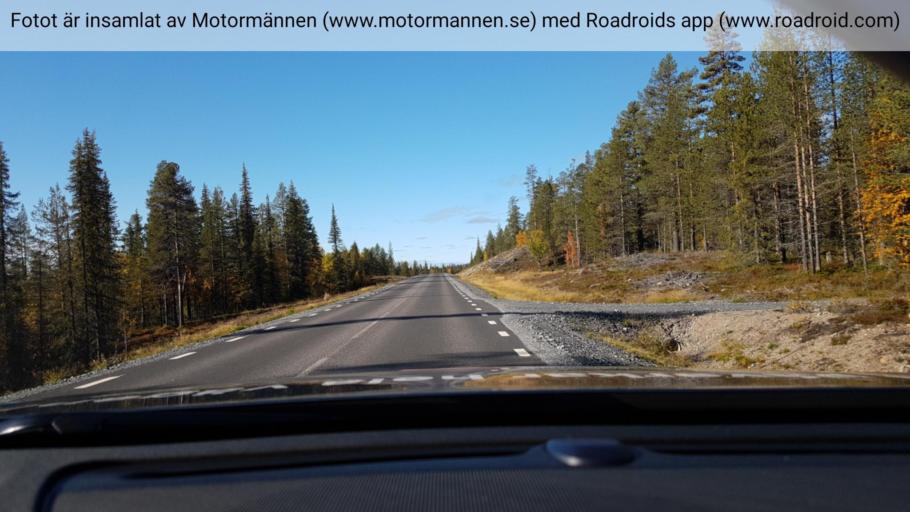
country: SE
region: Norrbotten
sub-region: Gallivare Kommun
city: Gaellivare
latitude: 66.9377
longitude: 20.8366
